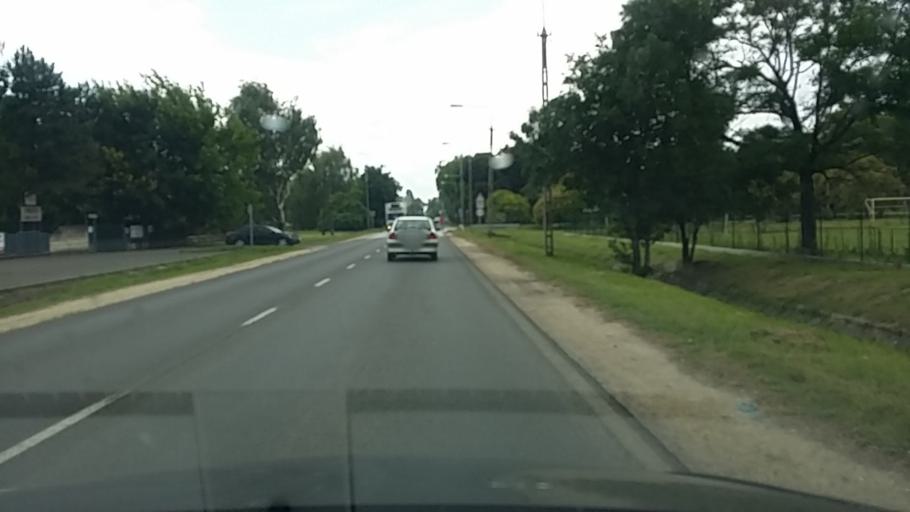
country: HU
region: Pest
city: Orkeny
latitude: 47.1249
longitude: 19.4324
